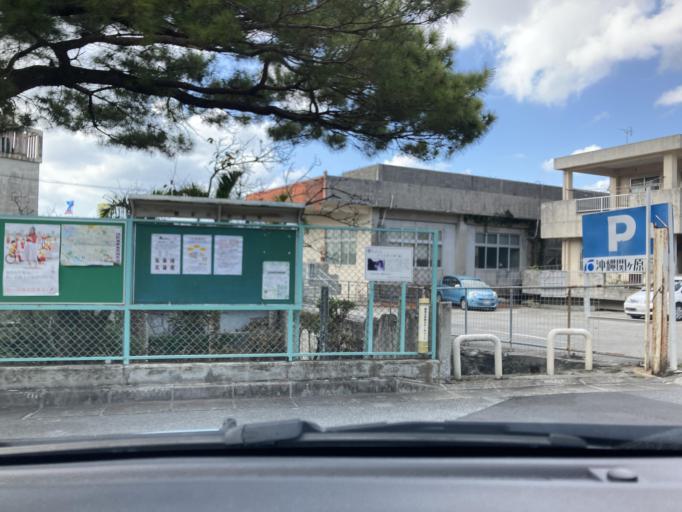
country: JP
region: Okinawa
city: Naha-shi
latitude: 26.2100
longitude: 127.7128
